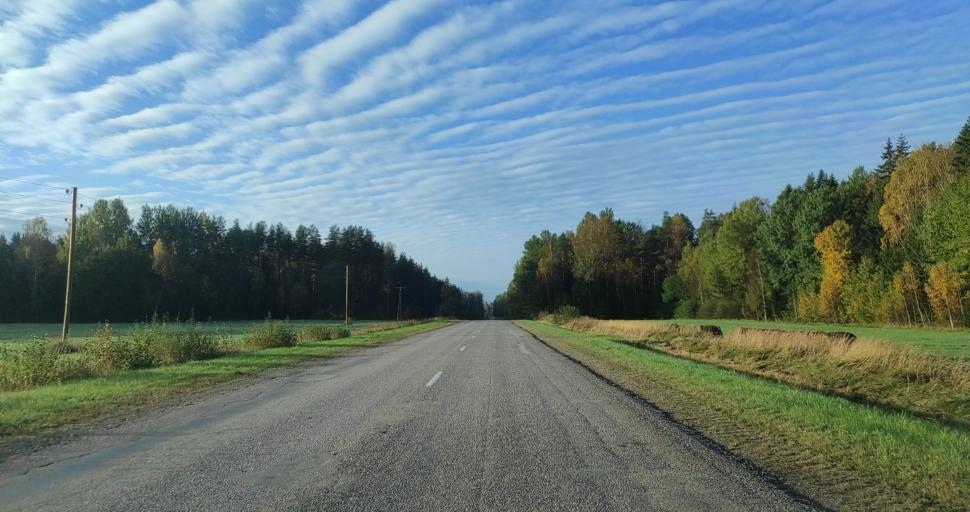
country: LV
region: Skrunda
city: Skrunda
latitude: 56.8013
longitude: 22.0069
